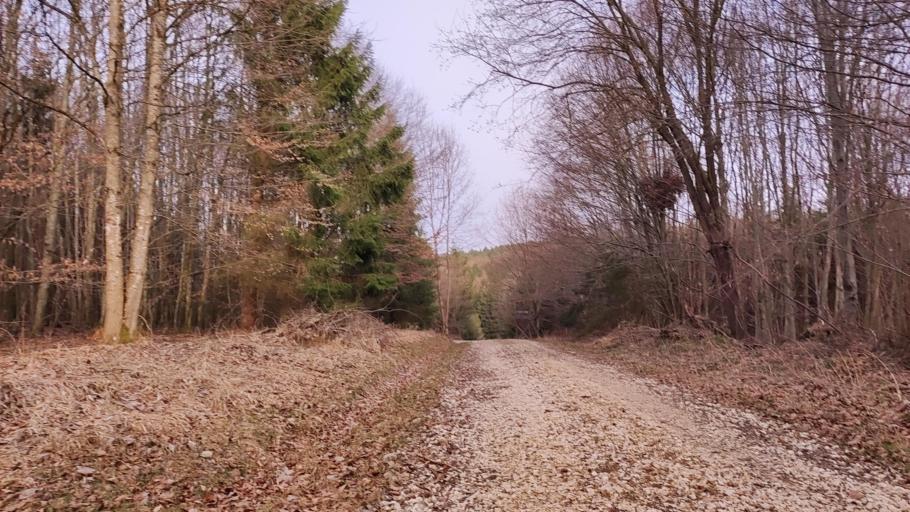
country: DE
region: Bavaria
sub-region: Swabia
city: Zusmarshausen
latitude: 48.4309
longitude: 10.6238
